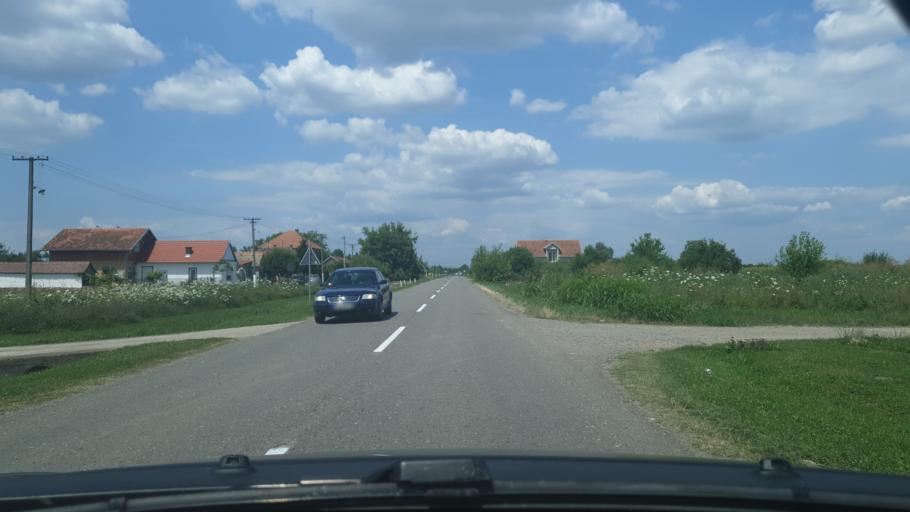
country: RS
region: Autonomna Pokrajina Vojvodina
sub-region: Sremski Okrug
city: Pecinci
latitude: 44.8500
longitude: 19.9617
